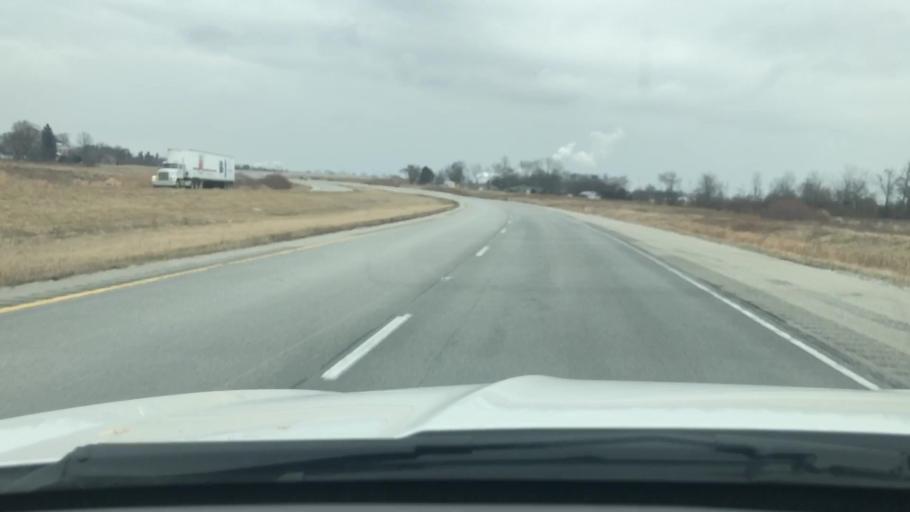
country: US
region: Indiana
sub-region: Cass County
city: Georgetown
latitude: 40.7019
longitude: -86.4599
